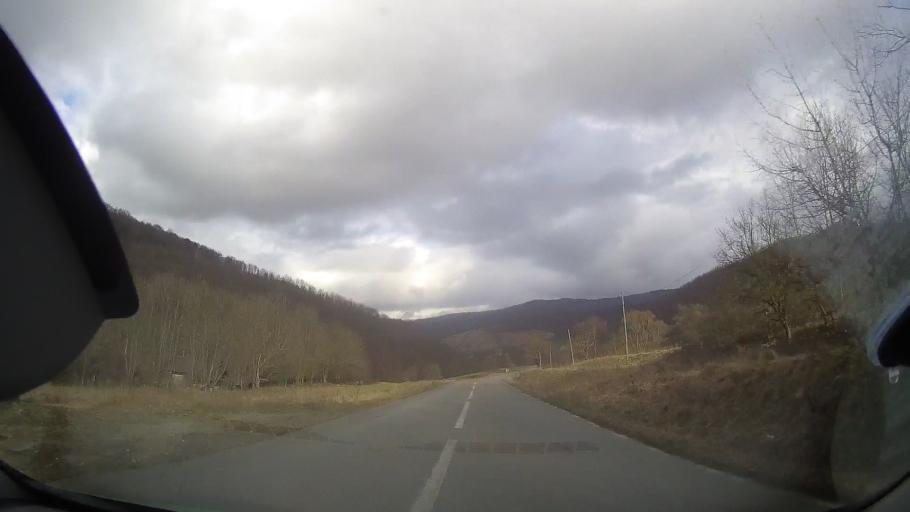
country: RO
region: Alba
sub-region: Comuna Rimetea
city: Rimetea
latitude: 46.4671
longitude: 23.5774
